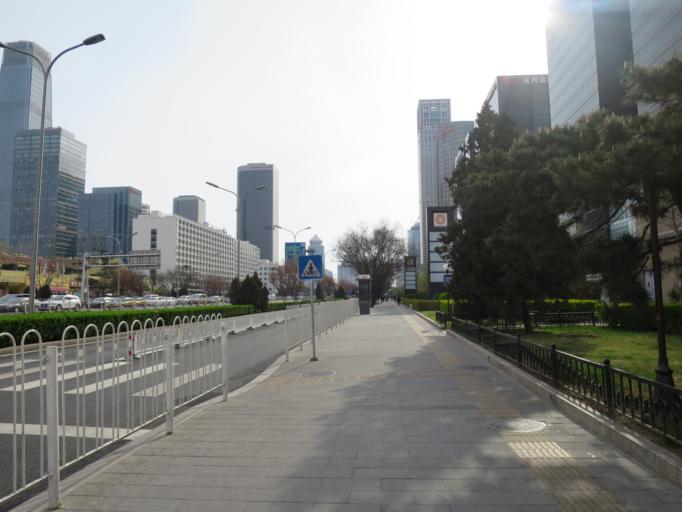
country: CN
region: Beijing
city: Chaowai
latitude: 39.9068
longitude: 116.4457
